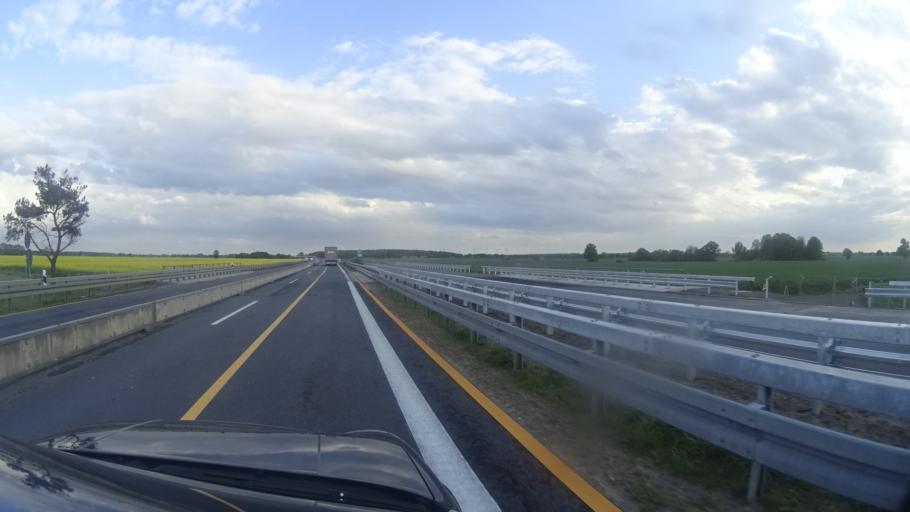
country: DE
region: Brandenburg
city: Wittstock
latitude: 53.2485
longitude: 12.4473
